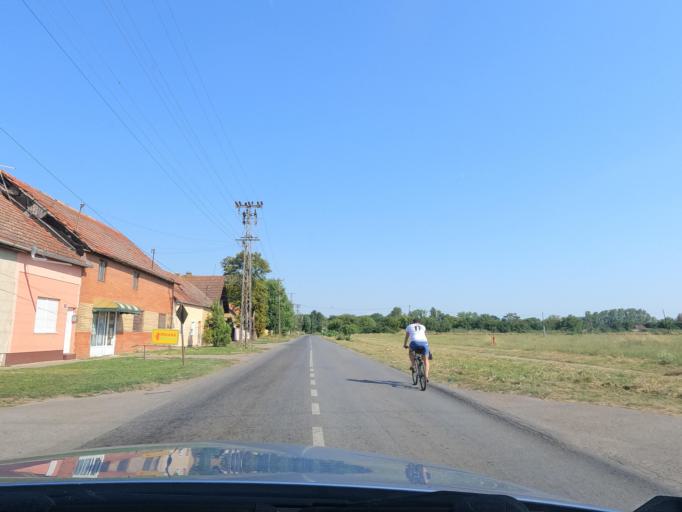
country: RS
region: Autonomna Pokrajina Vojvodina
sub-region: Juznobacki Okrug
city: Becej
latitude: 45.6240
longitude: 20.0313
